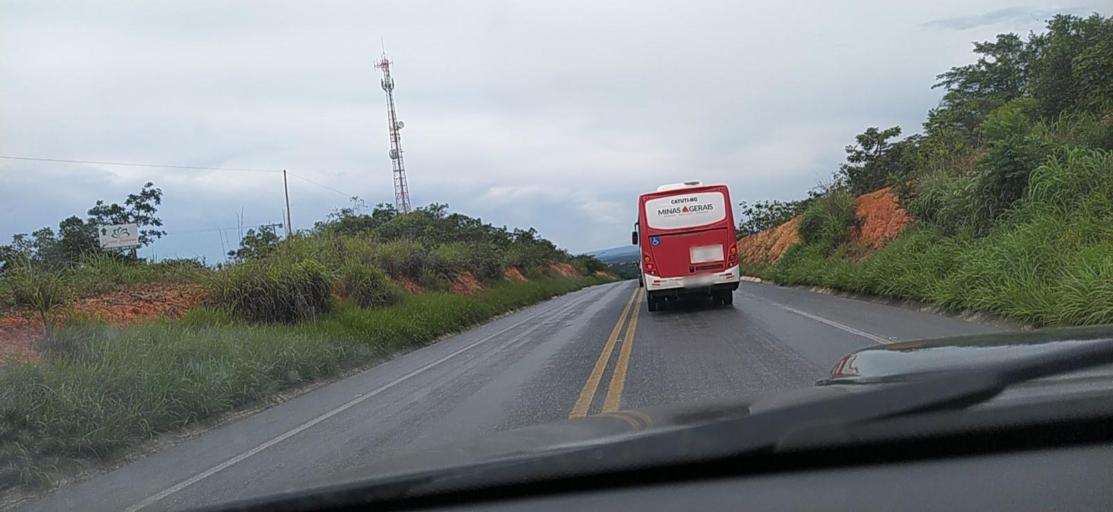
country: BR
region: Minas Gerais
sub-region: Montes Claros
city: Montes Claros
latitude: -16.6623
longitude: -43.7668
